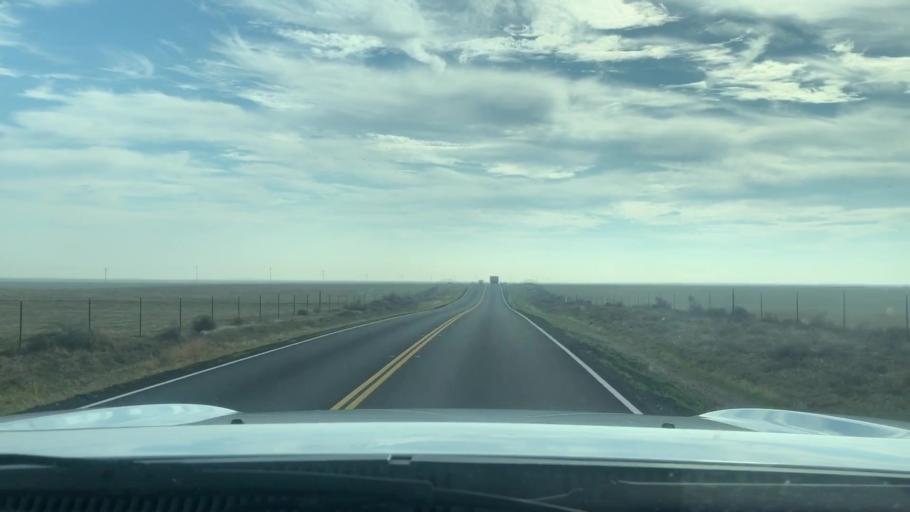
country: US
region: California
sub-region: Kern County
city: Lost Hills
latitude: 35.5993
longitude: -119.8485
